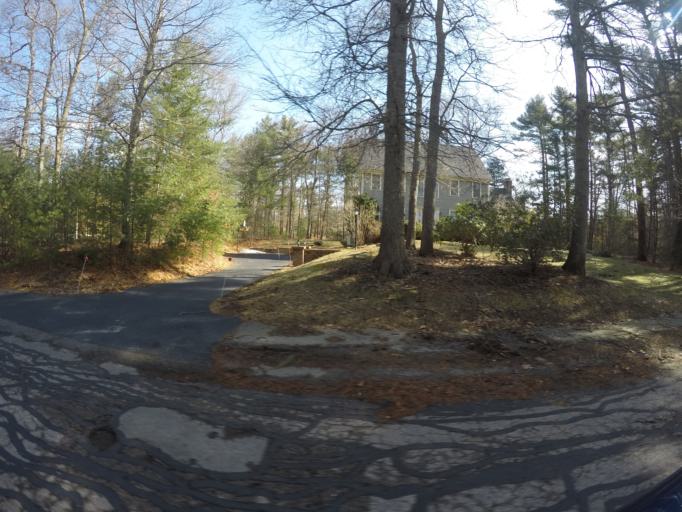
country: US
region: Massachusetts
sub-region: Bristol County
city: Easton
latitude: 42.0143
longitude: -71.1465
